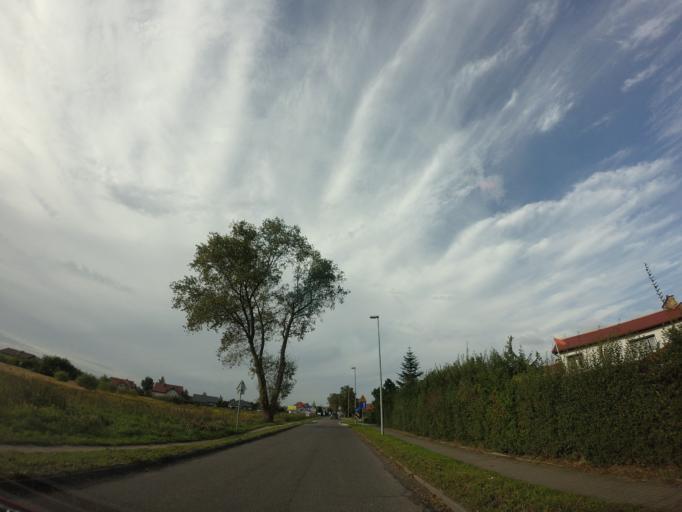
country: PL
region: West Pomeranian Voivodeship
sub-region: Powiat policki
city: Przeclaw
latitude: 53.4389
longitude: 14.4748
